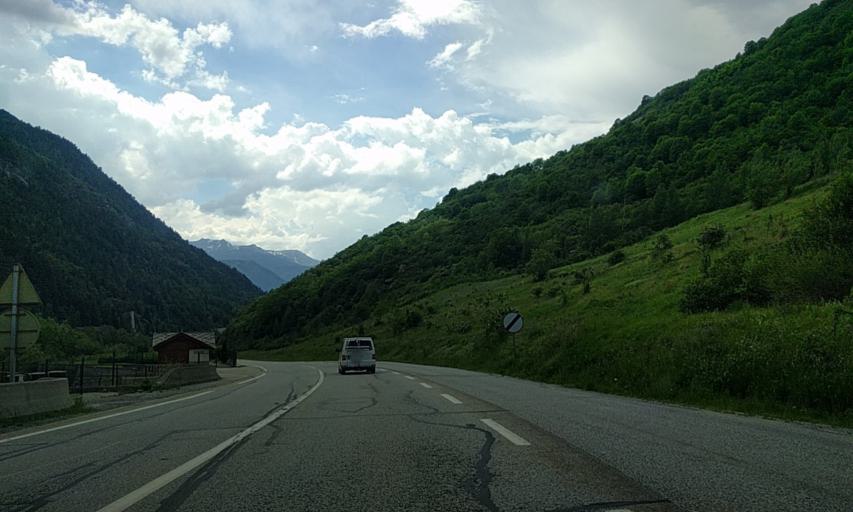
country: FR
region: Rhone-Alpes
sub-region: Departement de la Savoie
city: Saint-Michel-de-Maurienne
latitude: 45.2077
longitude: 6.5310
